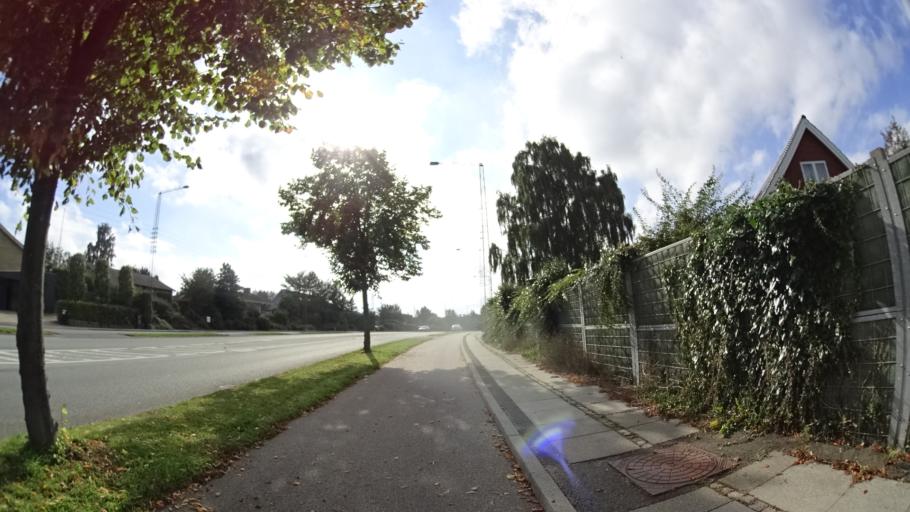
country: DK
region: Central Jutland
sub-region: Arhus Kommune
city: Arhus
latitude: 56.1249
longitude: 10.1810
